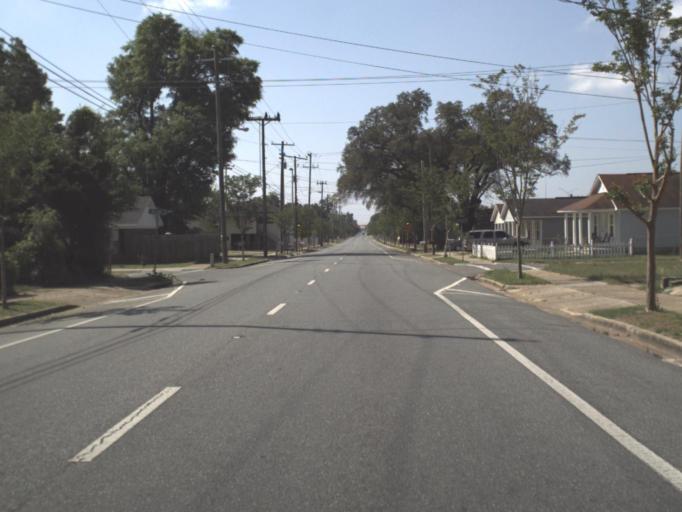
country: US
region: Florida
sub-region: Escambia County
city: Goulding
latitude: 30.4398
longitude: -87.2155
